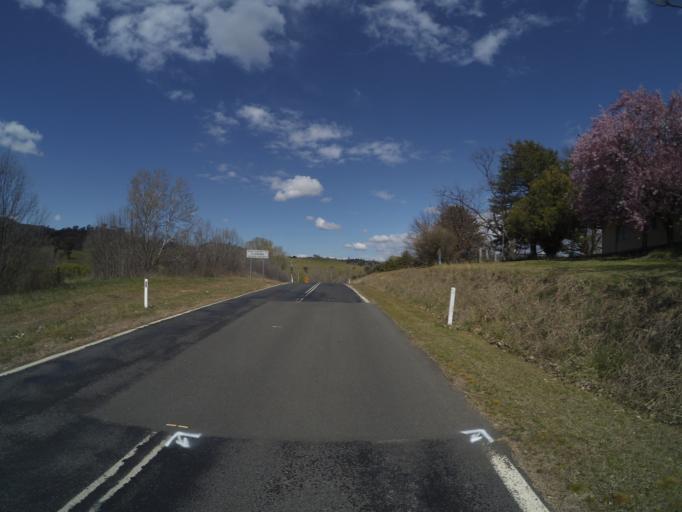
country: AU
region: Australian Capital Territory
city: Macarthur
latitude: -35.3942
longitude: 148.9608
